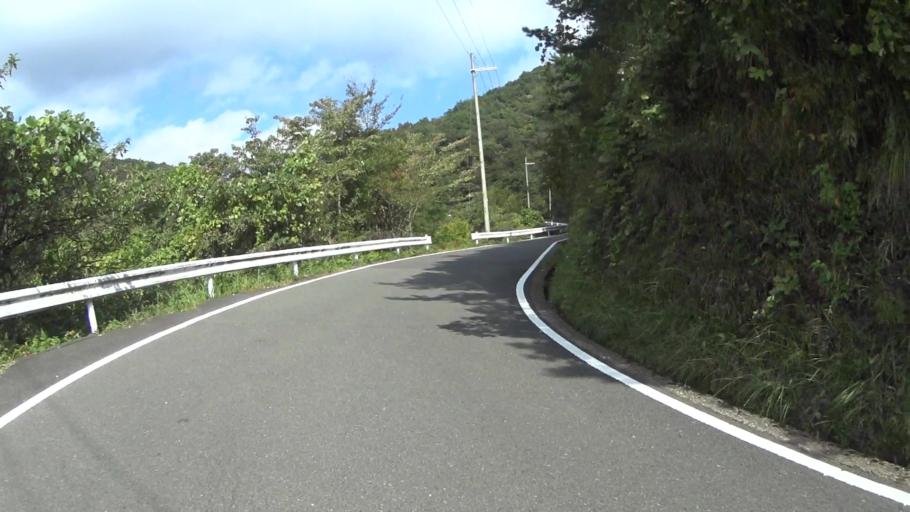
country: JP
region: Kyoto
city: Miyazu
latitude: 35.6767
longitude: 135.2661
